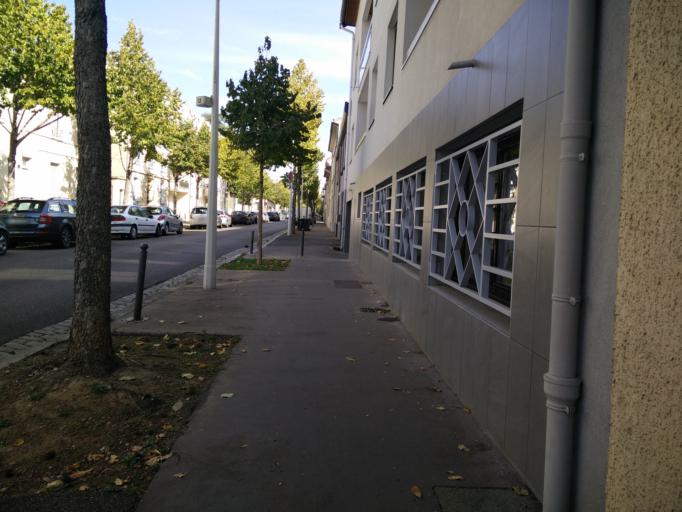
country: FR
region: Rhone-Alpes
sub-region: Departement du Rhone
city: Villeurbanne
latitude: 45.7481
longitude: 4.8824
